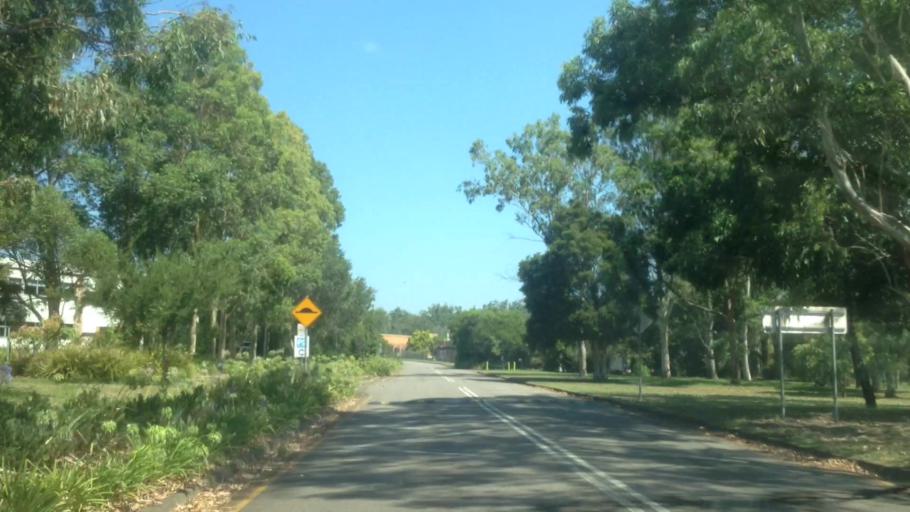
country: AU
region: New South Wales
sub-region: Lake Macquarie Shire
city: Cooranbong
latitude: -33.0856
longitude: 151.4595
